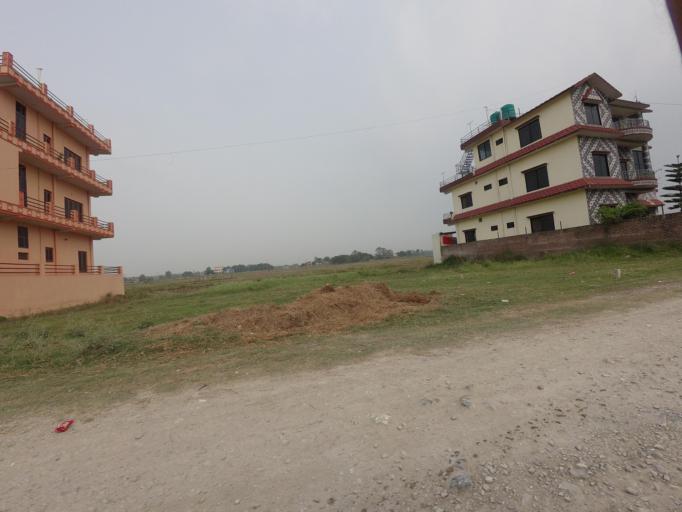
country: NP
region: Western Region
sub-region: Lumbini Zone
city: Bhairahawa
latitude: 27.5270
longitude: 83.4510
